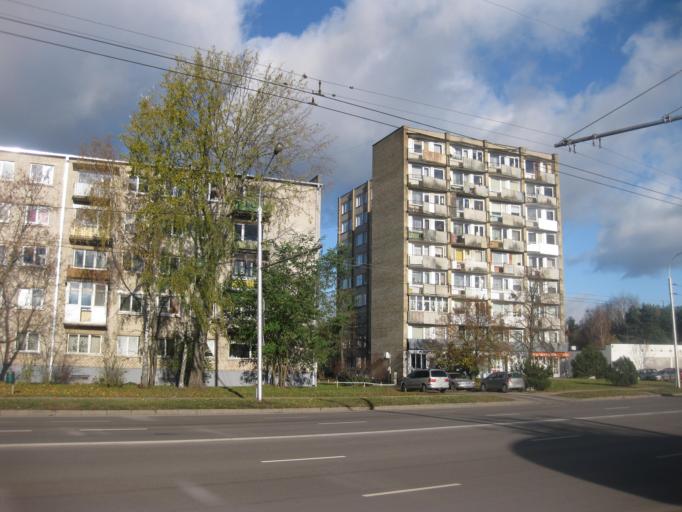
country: LT
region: Kauno apskritis
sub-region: Kaunas
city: Kaunas
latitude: 54.9146
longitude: 23.8993
